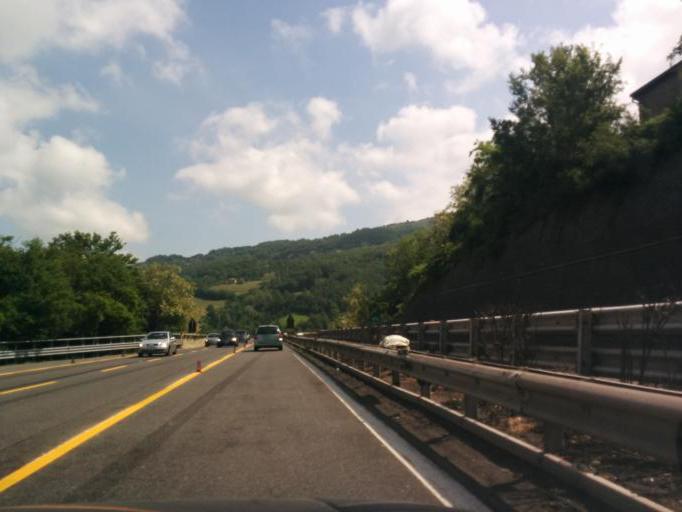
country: IT
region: Emilia-Romagna
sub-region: Provincia di Bologna
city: San Benedetto Val di Sambro
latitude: 44.1698
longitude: 11.2110
